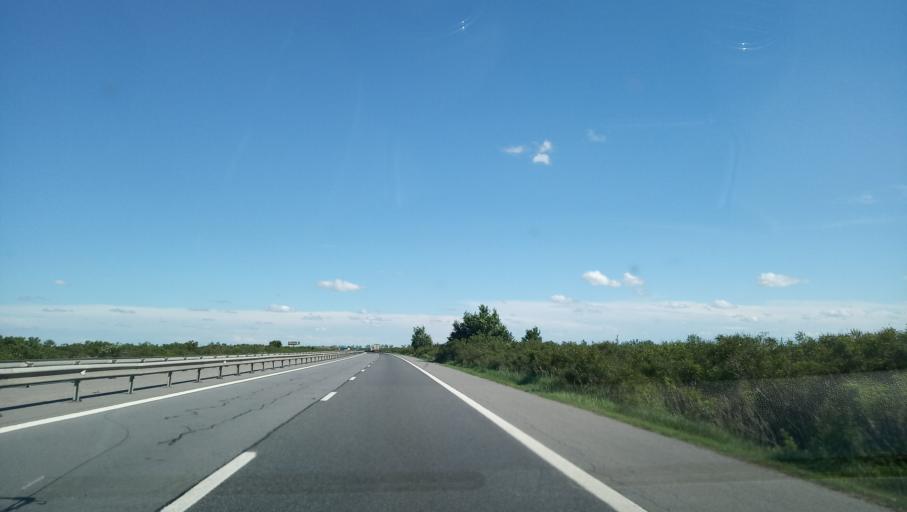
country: RO
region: Dambovita
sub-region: Comuna Corbii Mari
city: Corbii Mari
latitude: 44.5554
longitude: 25.4997
